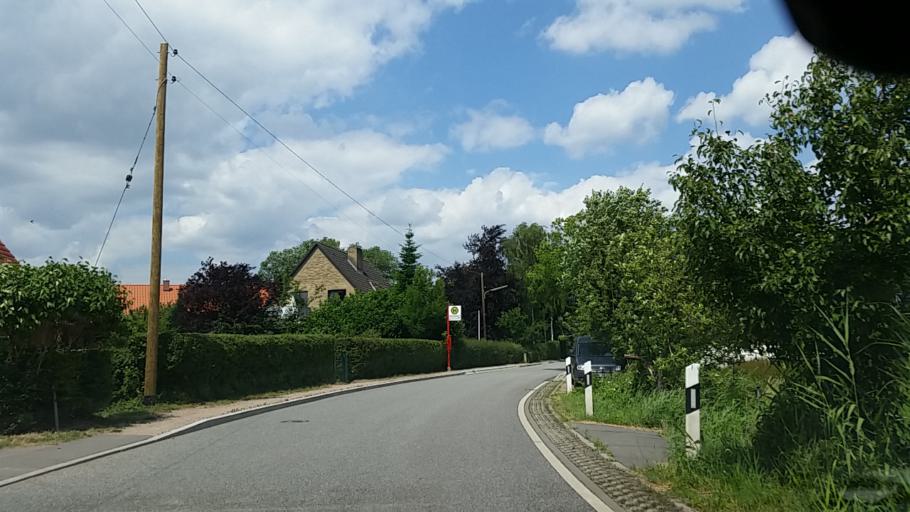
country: DE
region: Schleswig-Holstein
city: Oststeinbek
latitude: 53.5094
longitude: 10.1295
